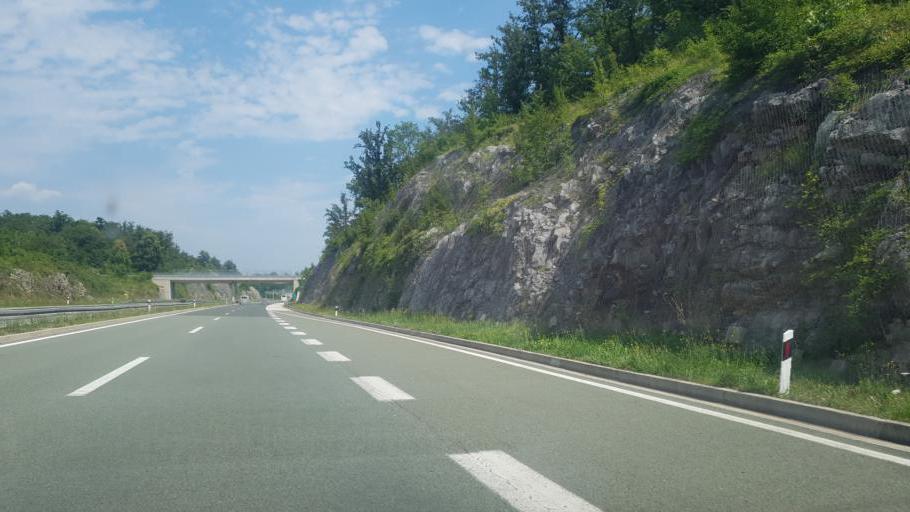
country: HR
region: Primorsko-Goranska
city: Matulji
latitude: 45.4004
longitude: 14.3004
